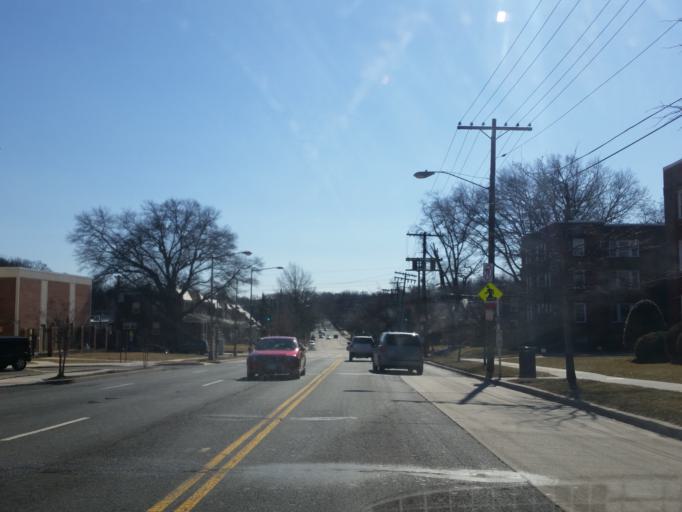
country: US
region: Maryland
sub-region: Prince George's County
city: Chillum
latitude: 38.9542
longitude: -77.0091
